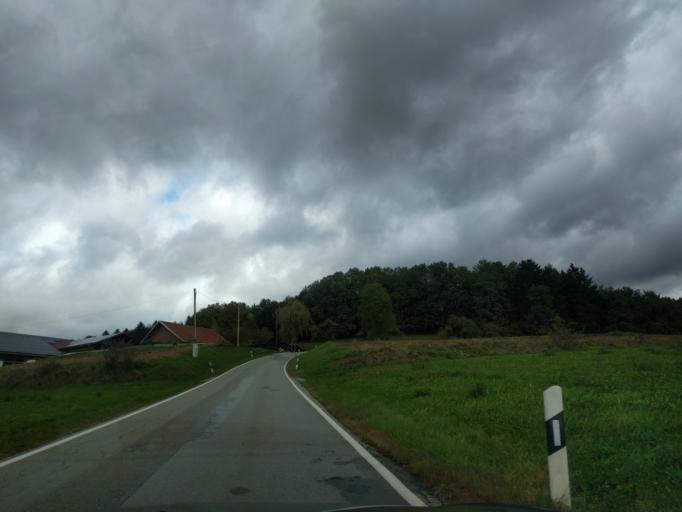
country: DE
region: Bavaria
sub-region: Lower Bavaria
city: Auerbach
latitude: 48.8328
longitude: 13.0923
